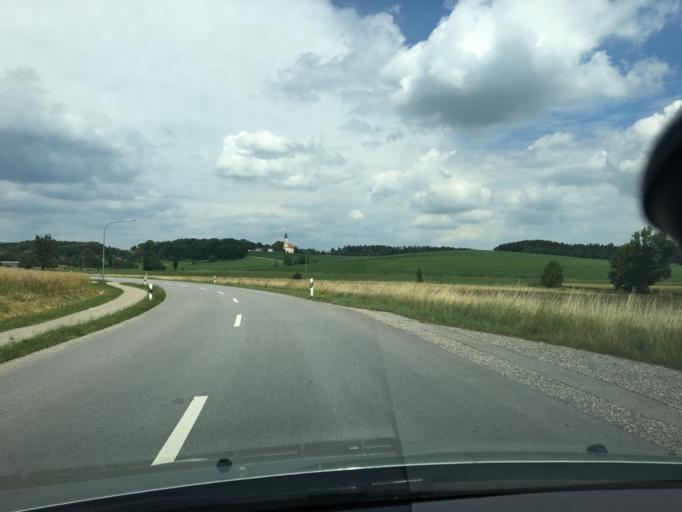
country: DE
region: Bavaria
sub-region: Upper Bavaria
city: Egglkofen
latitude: 48.4309
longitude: 12.4226
